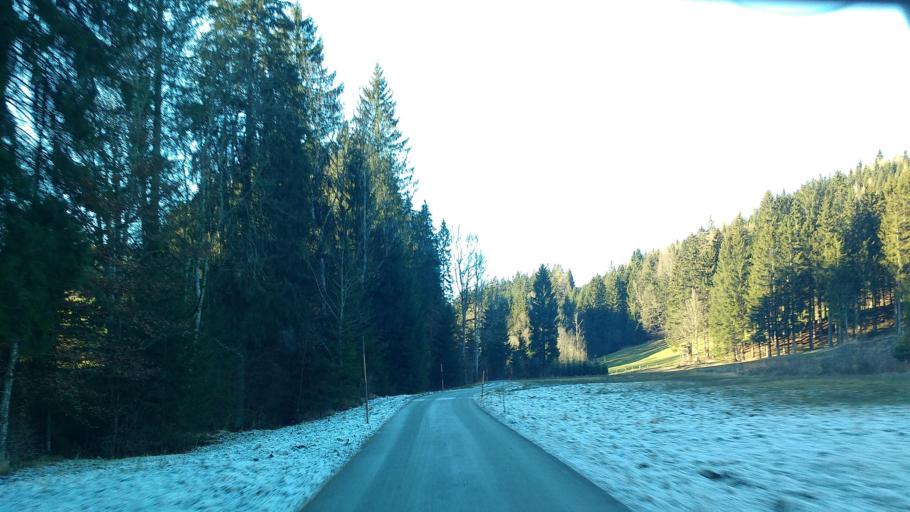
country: AT
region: Upper Austria
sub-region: Politischer Bezirk Kirchdorf an der Krems
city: Micheldorf in Oberoesterreich
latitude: 47.9019
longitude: 14.1796
